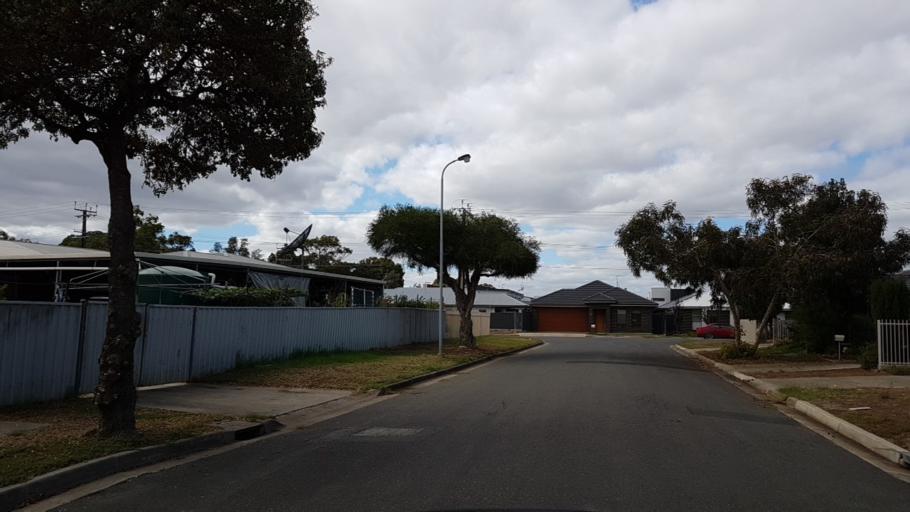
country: AU
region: South Australia
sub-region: Charles Sturt
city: Seaton
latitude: -34.9099
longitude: 138.5200
